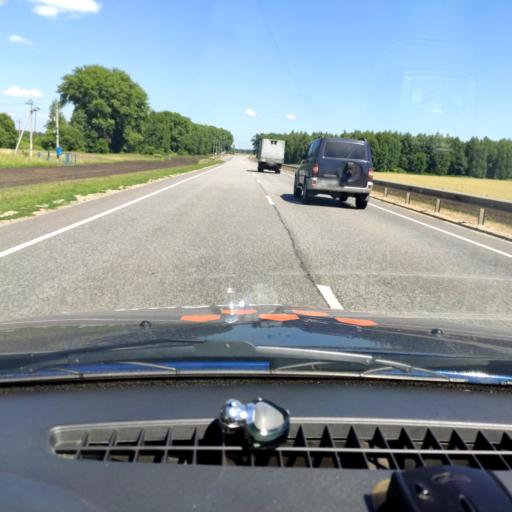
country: RU
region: Orjol
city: Pokrovskoye
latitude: 52.6411
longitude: 36.6607
